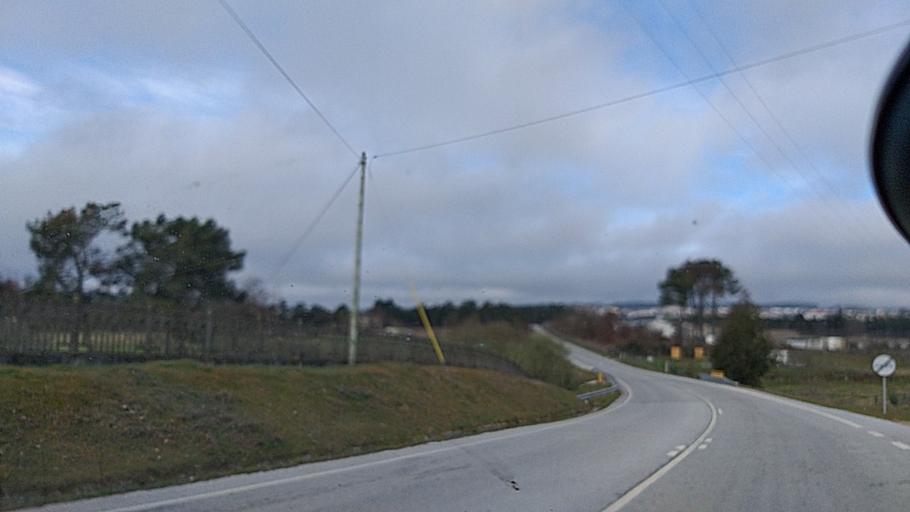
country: PT
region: Guarda
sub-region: Aguiar da Beira
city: Aguiar da Beira
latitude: 40.8065
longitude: -7.5268
